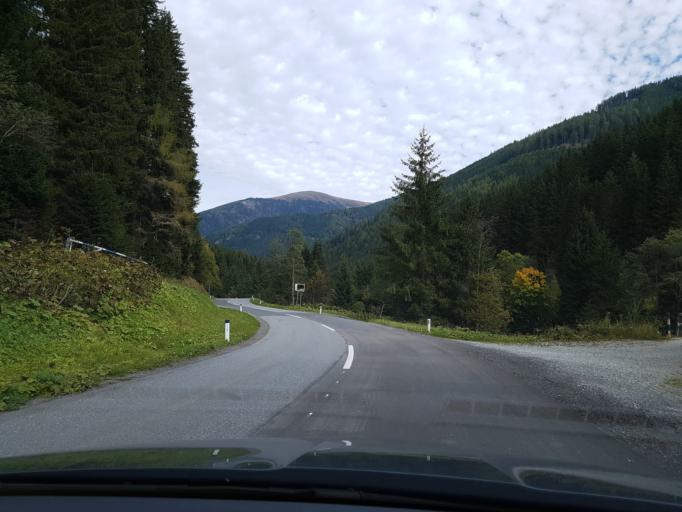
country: AT
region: Salzburg
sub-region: Politischer Bezirk Tamsweg
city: Ramingstein
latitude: 46.9748
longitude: 13.8981
